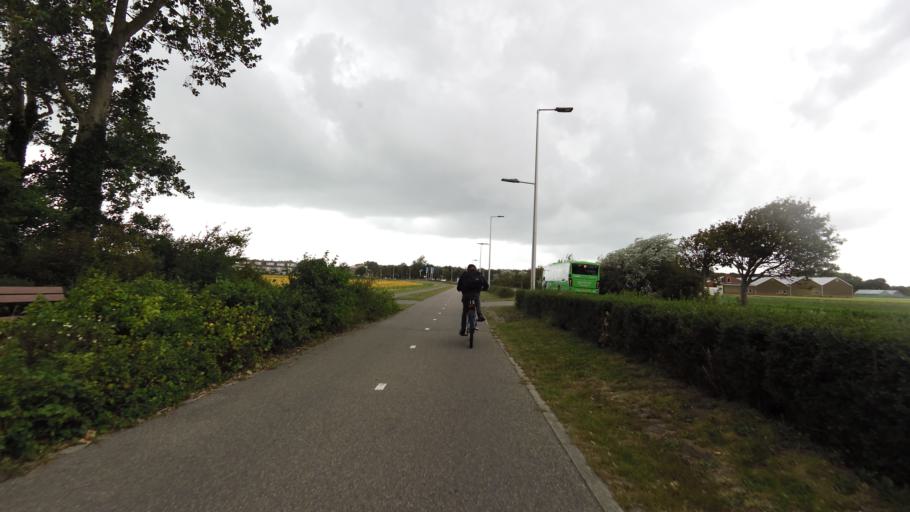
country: NL
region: South Holland
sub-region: Gemeente Noordwijk
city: Noordwijk-Binnen
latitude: 52.2478
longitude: 4.4516
